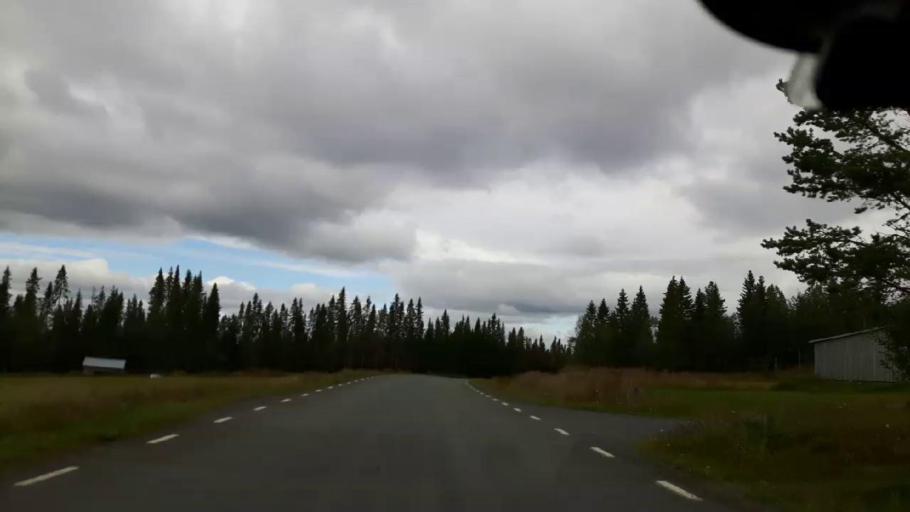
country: SE
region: Jaemtland
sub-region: Krokoms Kommun
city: Valla
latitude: 63.5440
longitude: 13.8557
